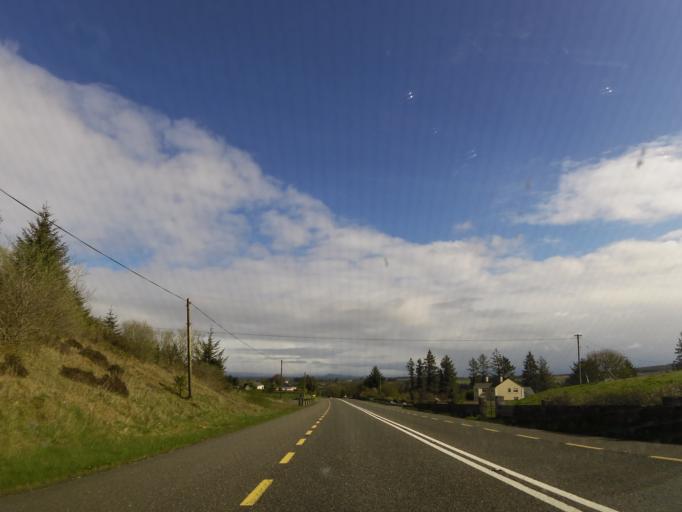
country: IE
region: Connaught
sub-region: Sligo
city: Tobercurry
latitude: 53.9221
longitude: -8.7856
